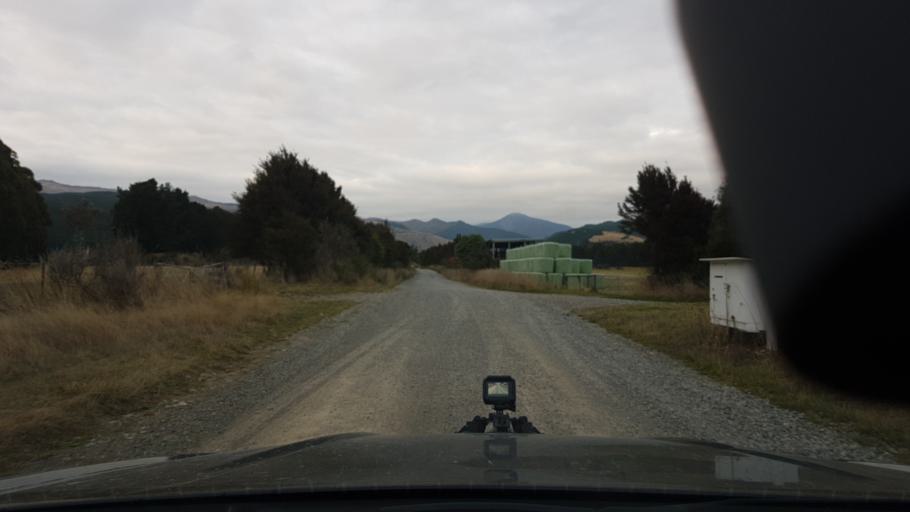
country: NZ
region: Tasman
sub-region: Tasman District
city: Brightwater
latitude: -41.6681
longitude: 173.1937
